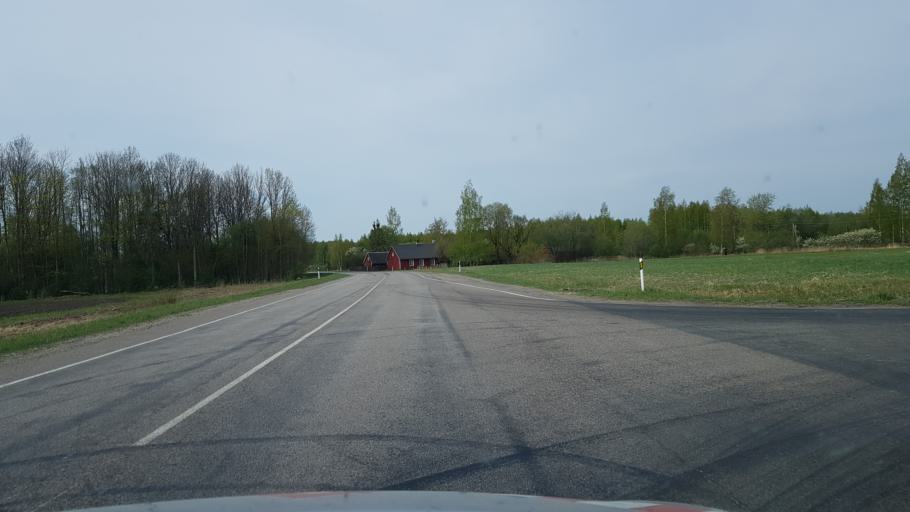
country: EE
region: Paernumaa
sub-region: Audru vald
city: Audru
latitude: 58.3928
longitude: 24.2794
